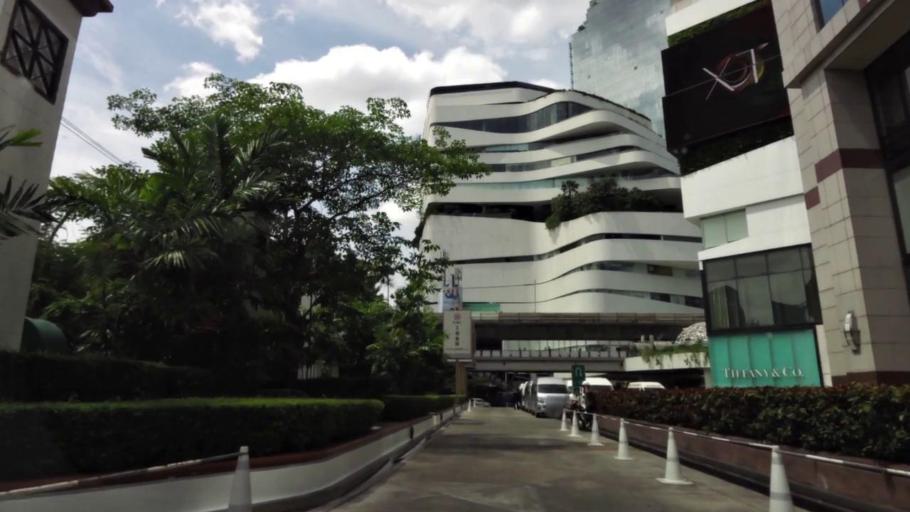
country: TH
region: Bangkok
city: Khlong Toei
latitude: 13.7304
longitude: 100.5683
